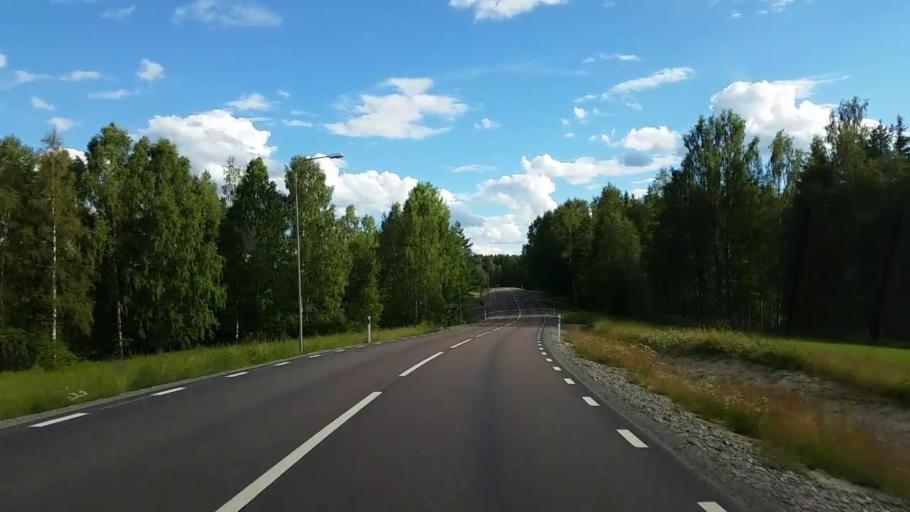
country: SE
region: Gaevleborg
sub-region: Ljusdals Kommun
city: Ljusdal
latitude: 61.8435
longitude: 16.0025
